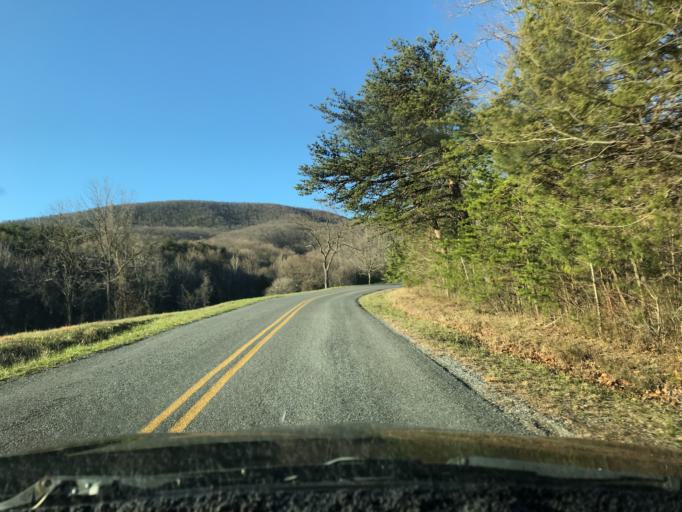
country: US
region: Virginia
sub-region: Botetourt County
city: Buchanan
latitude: 37.4705
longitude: -79.6588
